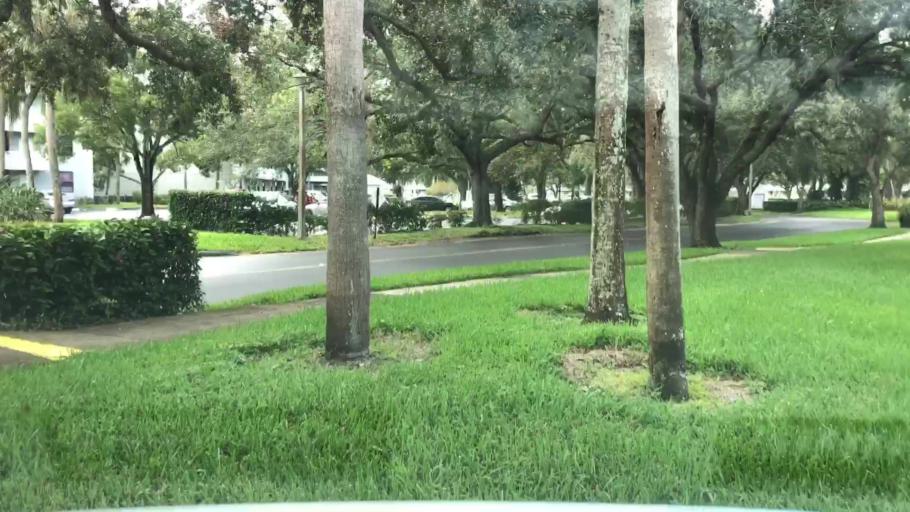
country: US
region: Florida
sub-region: Broward County
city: Pine Island Ridge
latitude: 26.0993
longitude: -80.2699
